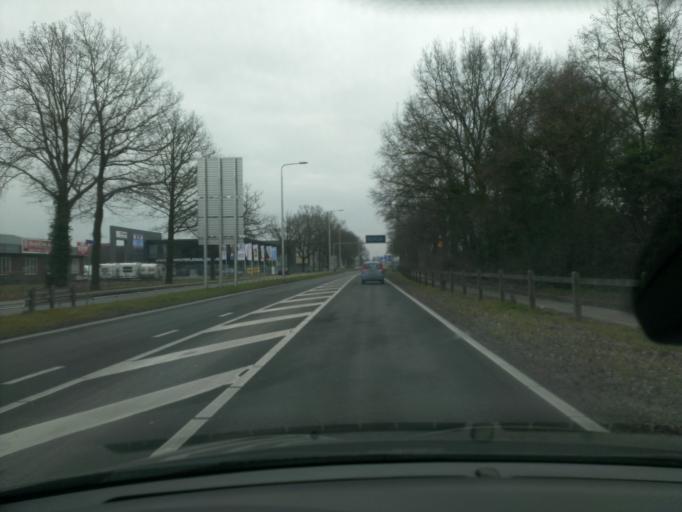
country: NL
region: Overijssel
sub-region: Gemeente Almelo
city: Almelo
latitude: 52.3479
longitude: 6.6790
